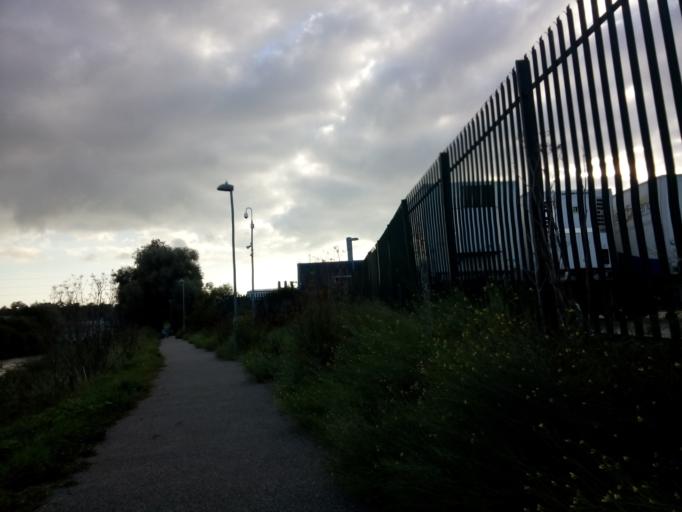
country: GB
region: England
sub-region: Suffolk
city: Bramford
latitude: 52.0633
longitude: 1.1241
